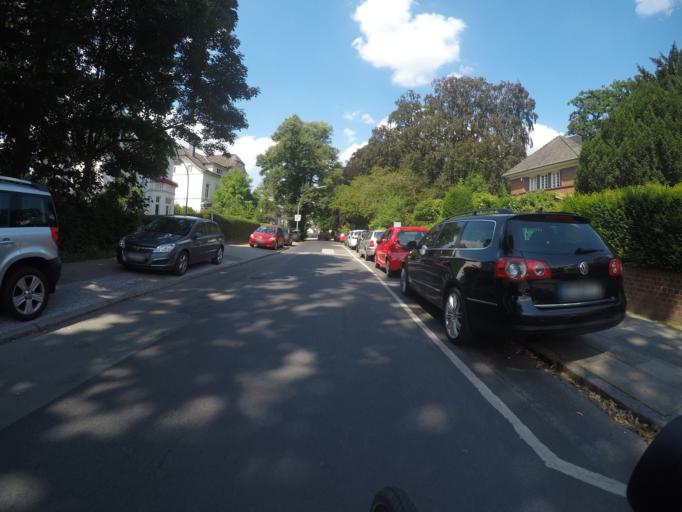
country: DE
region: Hamburg
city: Bergedorf
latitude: 53.4898
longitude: 10.2154
